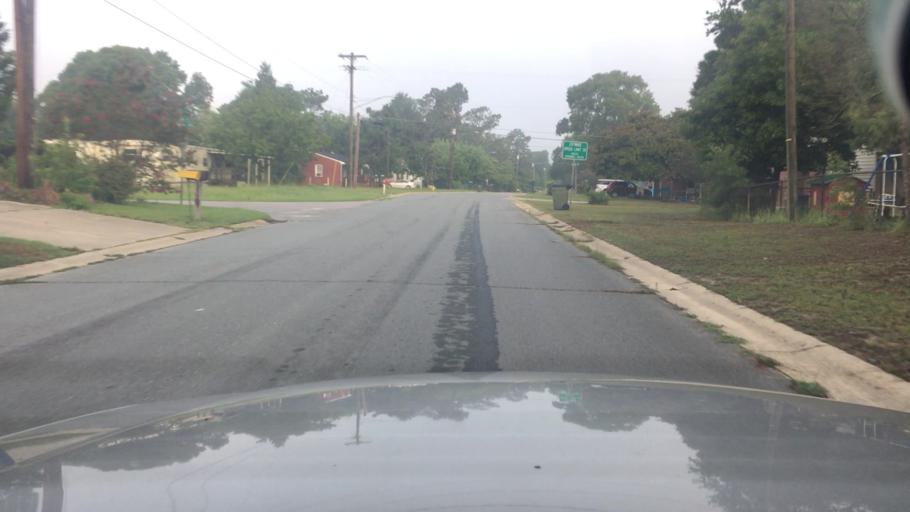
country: US
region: North Carolina
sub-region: Cumberland County
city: Hope Mills
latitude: 35.0181
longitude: -78.9254
